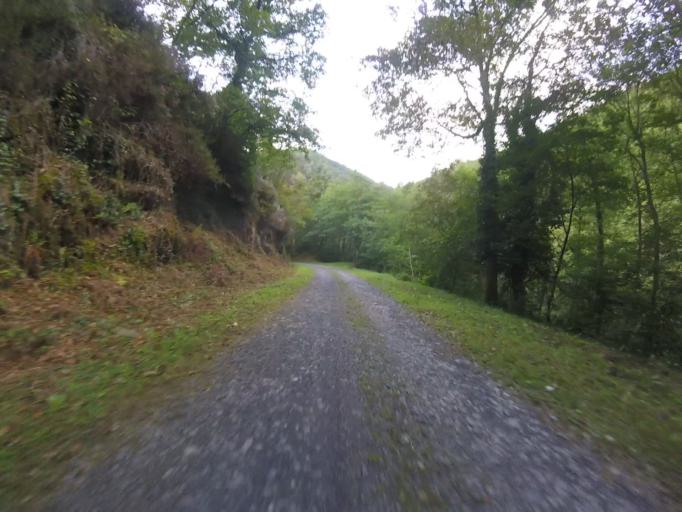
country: ES
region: Basque Country
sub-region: Provincia de Guipuzcoa
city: Berastegui
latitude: 43.1506
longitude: -1.9643
